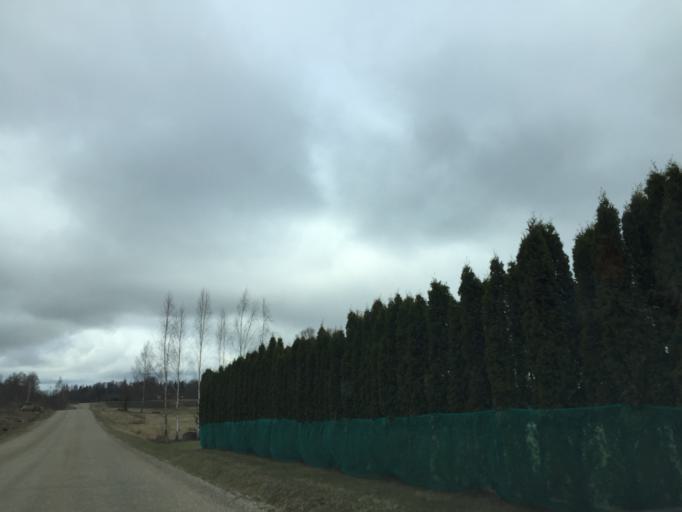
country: LV
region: Ilukste
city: Ilukste
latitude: 56.0464
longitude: 26.1902
